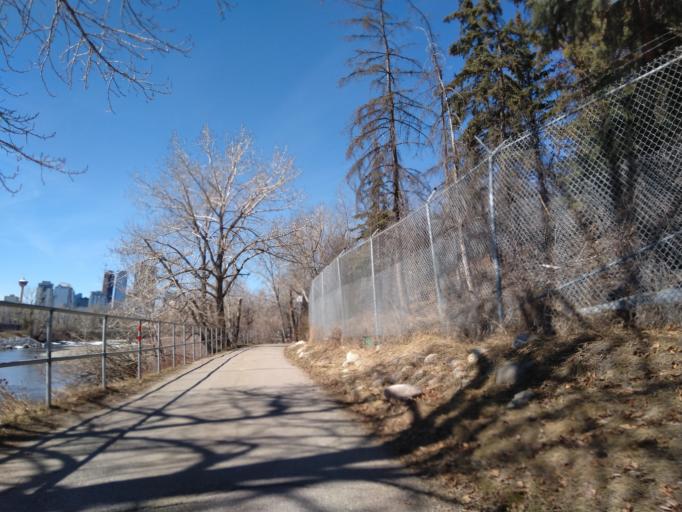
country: CA
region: Alberta
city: Calgary
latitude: 51.0470
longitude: -114.0321
